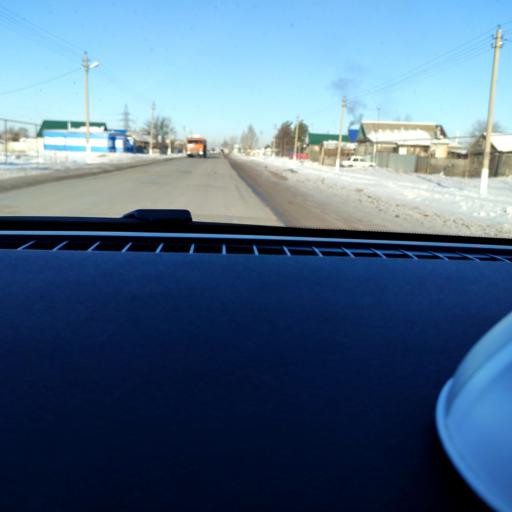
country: RU
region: Samara
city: Spiridonovka
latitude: 53.1041
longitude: 50.6454
